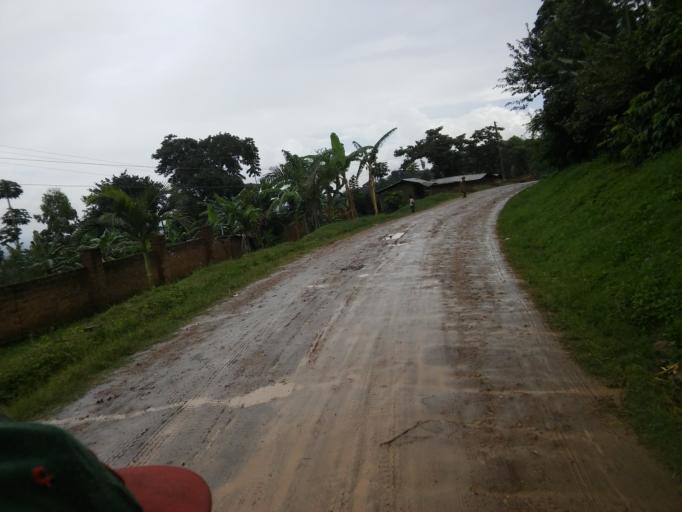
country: UG
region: Eastern Region
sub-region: Mbale District
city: Mbale
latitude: 1.0198
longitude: 34.2201
